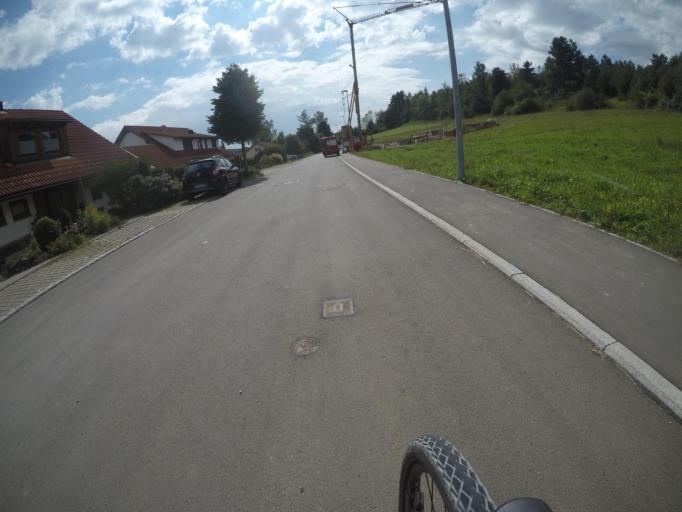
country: DE
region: Baden-Wuerttemberg
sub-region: Tuebingen Region
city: Munsingen
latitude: 48.4183
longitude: 9.4988
